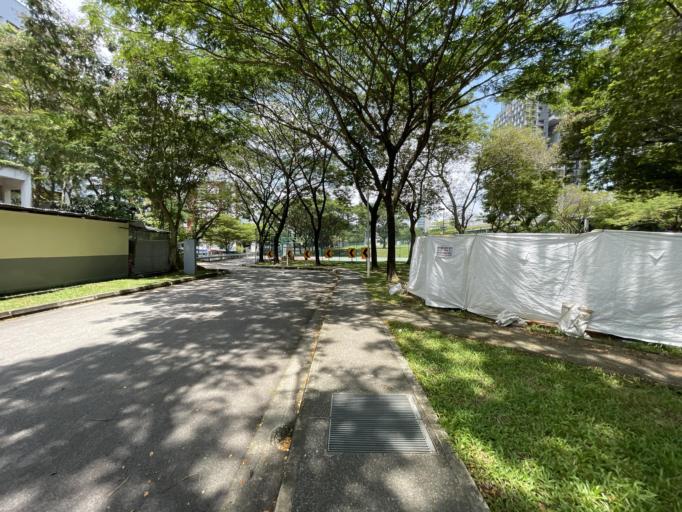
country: SG
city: Singapore
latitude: 1.3029
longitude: 103.7686
